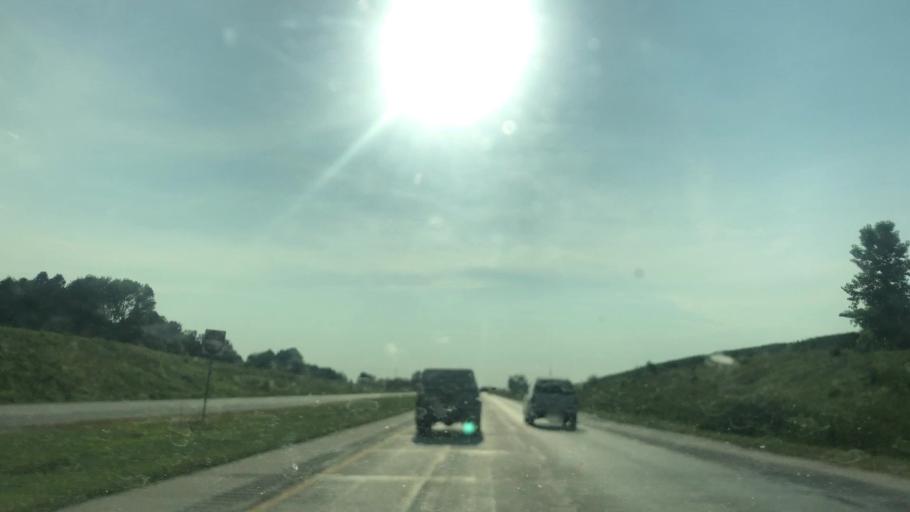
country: US
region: Iowa
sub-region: Story County
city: Nevada
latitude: 42.0058
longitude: -93.4537
